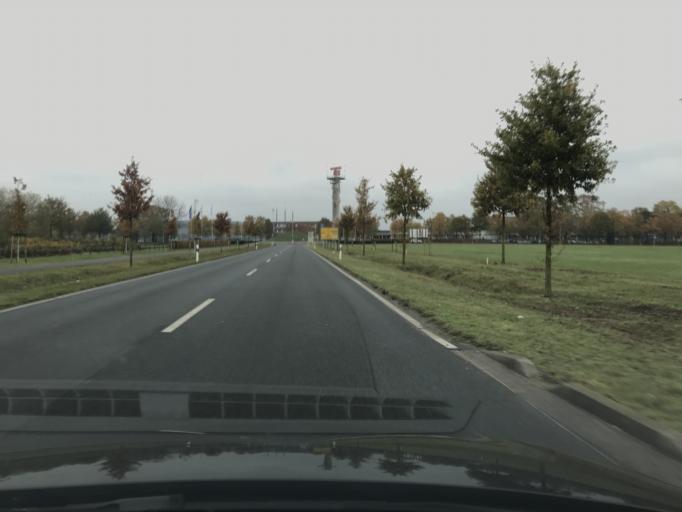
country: DE
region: North Rhine-Westphalia
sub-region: Regierungsbezirk Munster
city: Ladbergen
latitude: 52.1276
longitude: 7.6922
